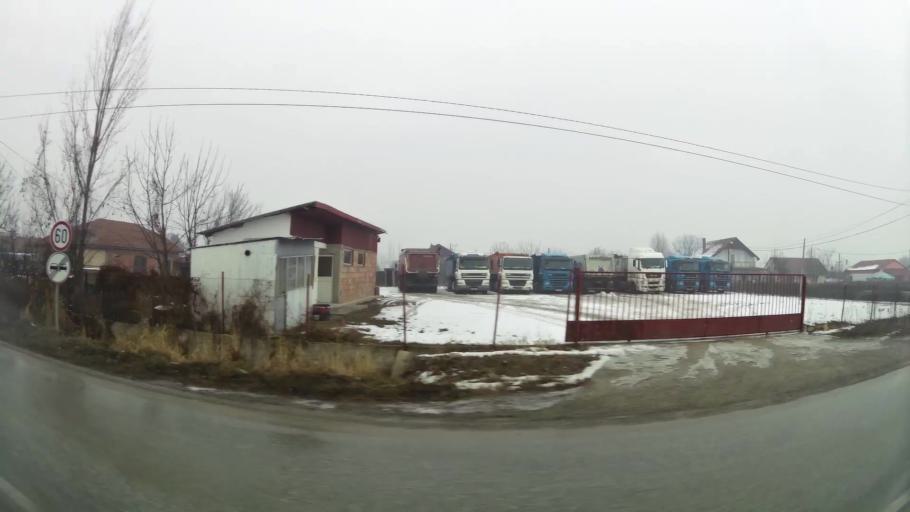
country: MK
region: Ilinden
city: Idrizovo
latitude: 41.9494
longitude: 21.5885
